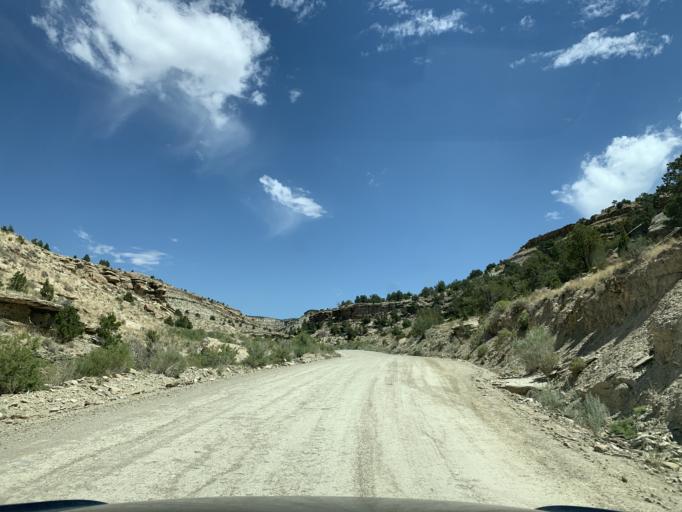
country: US
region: Utah
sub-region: Carbon County
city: East Carbon City
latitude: 39.8408
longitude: -110.2546
